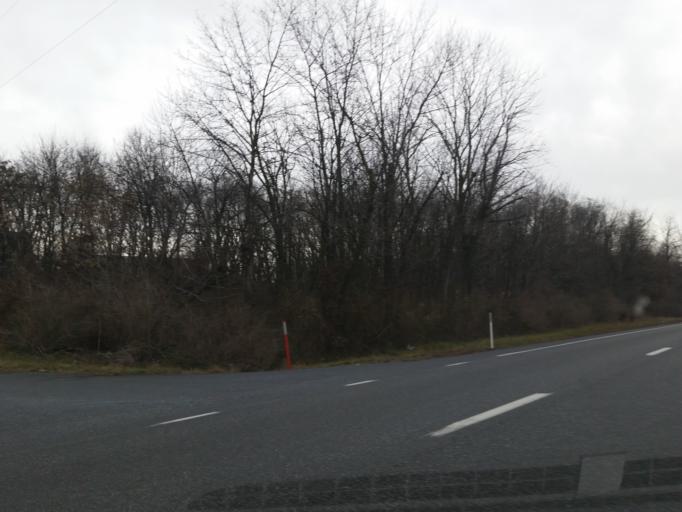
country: US
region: Pennsylvania
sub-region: Dauphin County
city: Palmdale
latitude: 40.3750
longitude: -76.6446
